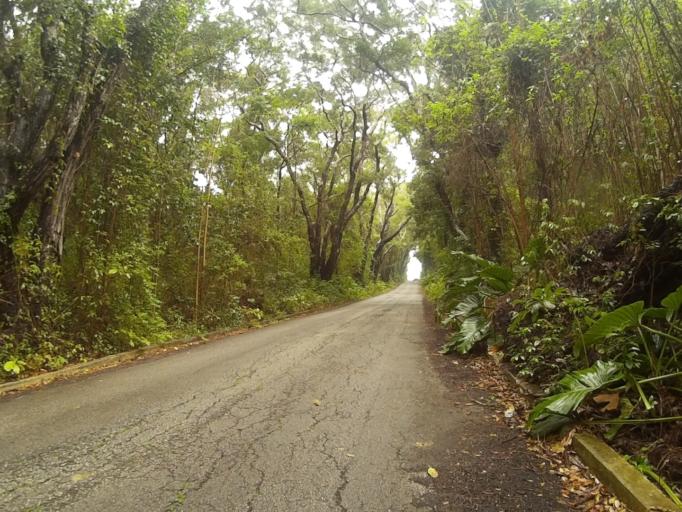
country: BB
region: Saint Andrew
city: Greenland
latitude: 13.2749
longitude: -59.5867
